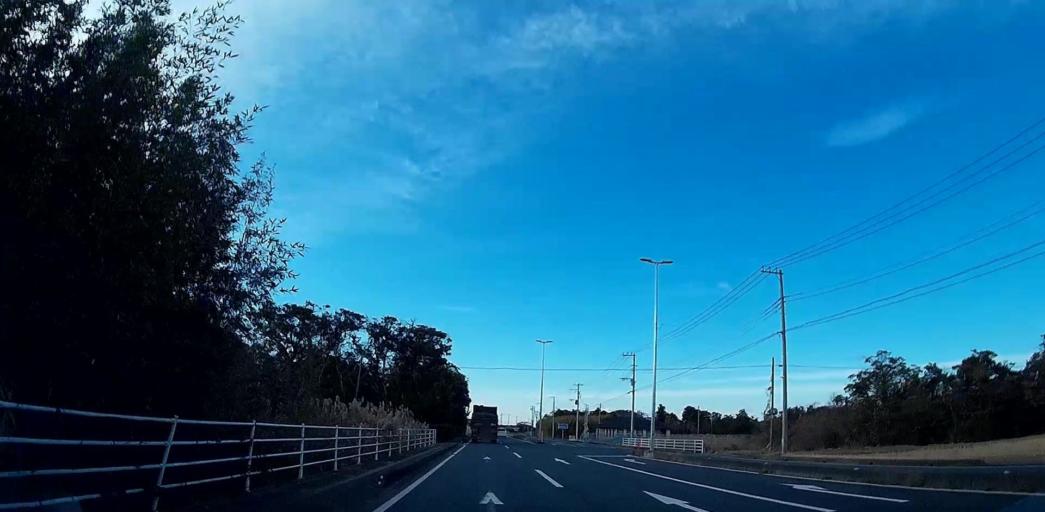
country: JP
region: Chiba
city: Omigawa
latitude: 35.8244
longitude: 140.7269
